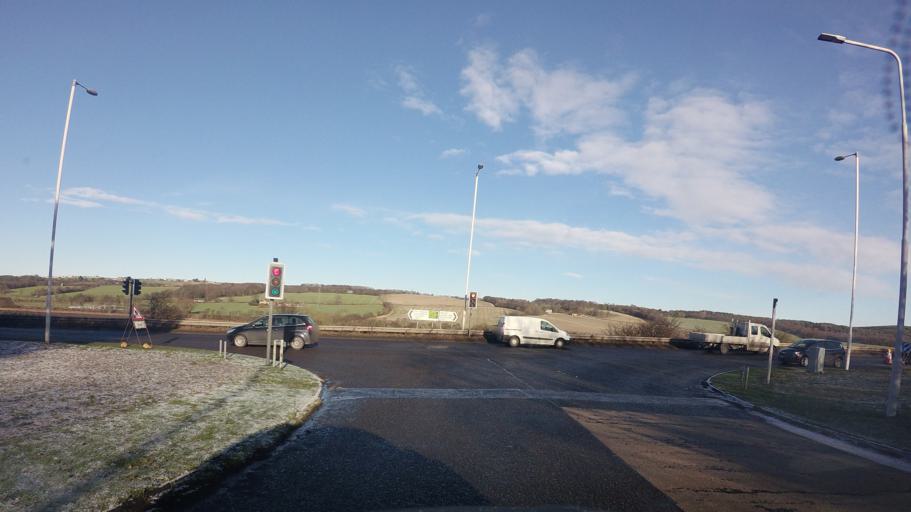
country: GB
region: Scotland
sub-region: Fife
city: Inverkeithing
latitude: 56.0382
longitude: -3.3807
